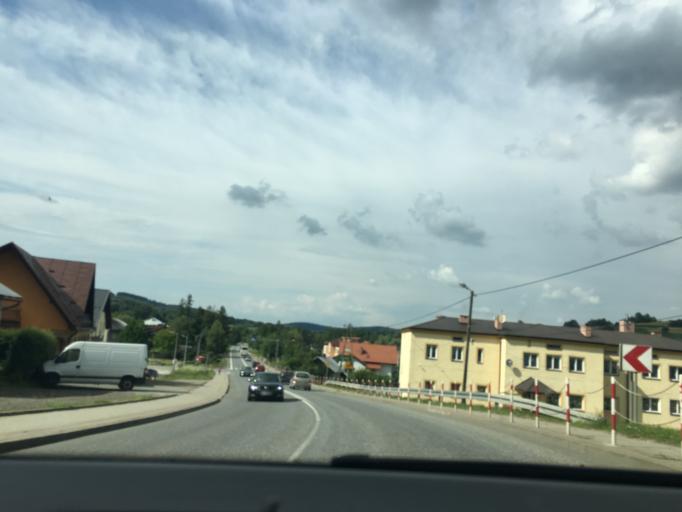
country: PL
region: Subcarpathian Voivodeship
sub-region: Powiat strzyzowski
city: Niebylec
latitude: 49.8569
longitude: 21.9039
